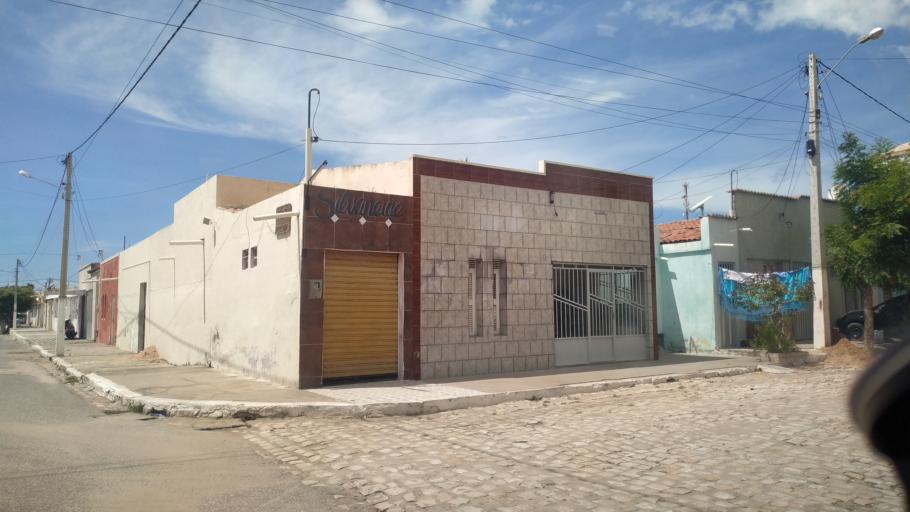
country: BR
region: Rio Grande do Norte
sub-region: Areia Branca
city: Areia Branca
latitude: -4.9539
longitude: -37.1305
